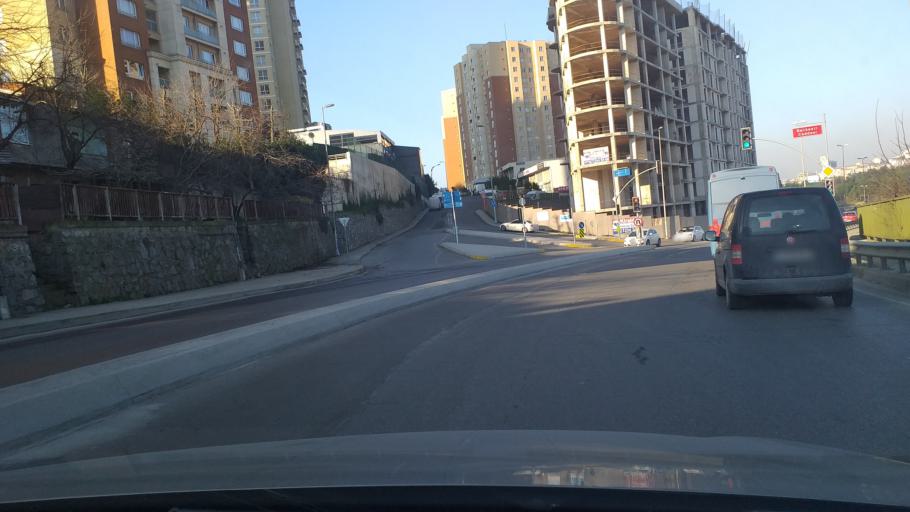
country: TR
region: Istanbul
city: Maltepe
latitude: 40.9210
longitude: 29.1864
